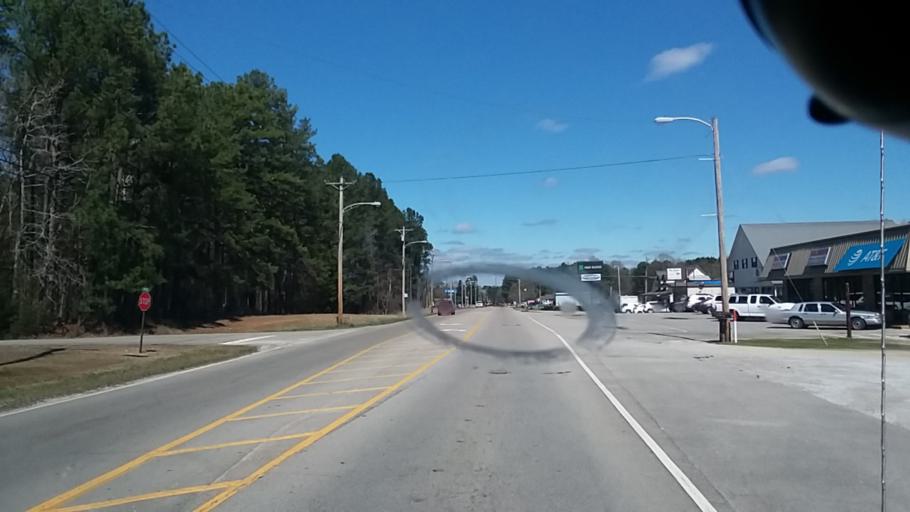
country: US
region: Mississippi
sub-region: Tishomingo County
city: Iuka
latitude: 34.8012
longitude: -88.2045
